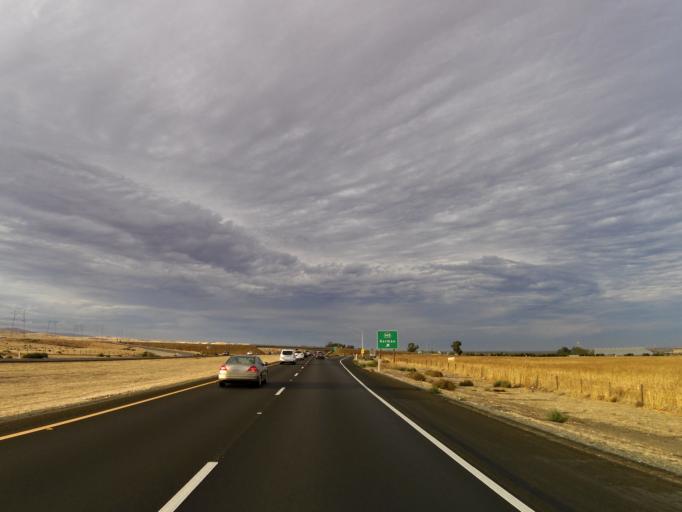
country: US
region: California
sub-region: Fresno County
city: Coalinga
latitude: 36.2909
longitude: -120.2668
